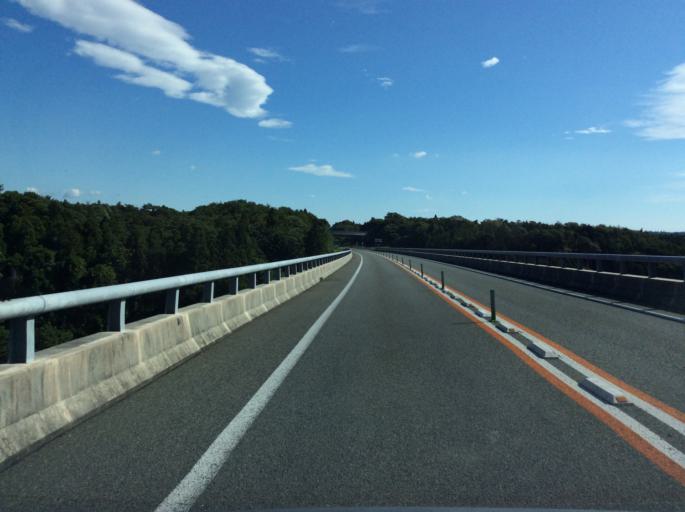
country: JP
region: Fukushima
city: Iwaki
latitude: 37.2491
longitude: 140.9896
